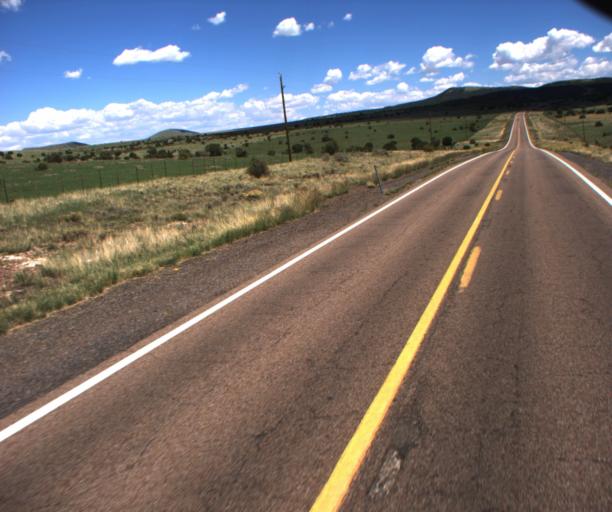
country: US
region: Arizona
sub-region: Navajo County
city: Pinetop-Lakeside
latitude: 34.2706
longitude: -109.6457
